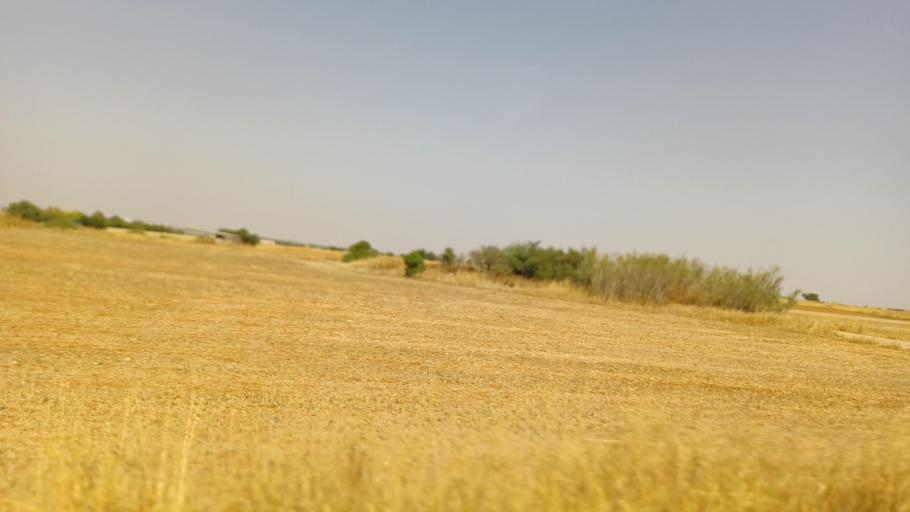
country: CY
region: Ammochostos
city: Avgorou
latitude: 35.0455
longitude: 33.8512
